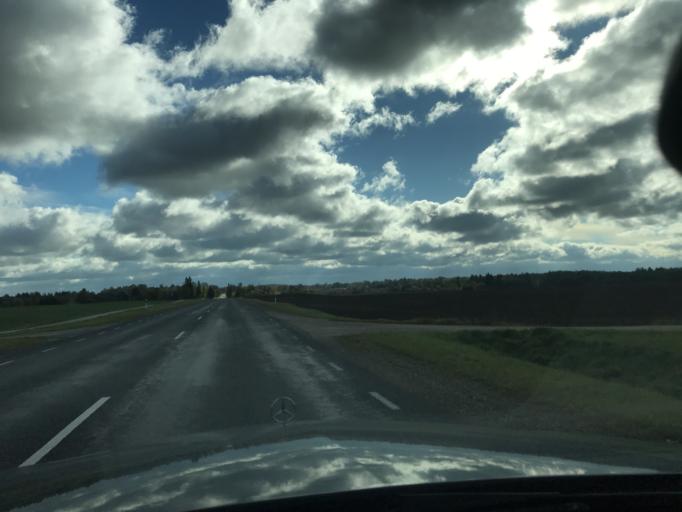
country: EE
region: Vorumaa
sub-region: Antsla vald
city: Vana-Antsla
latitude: 57.9524
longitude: 26.2832
